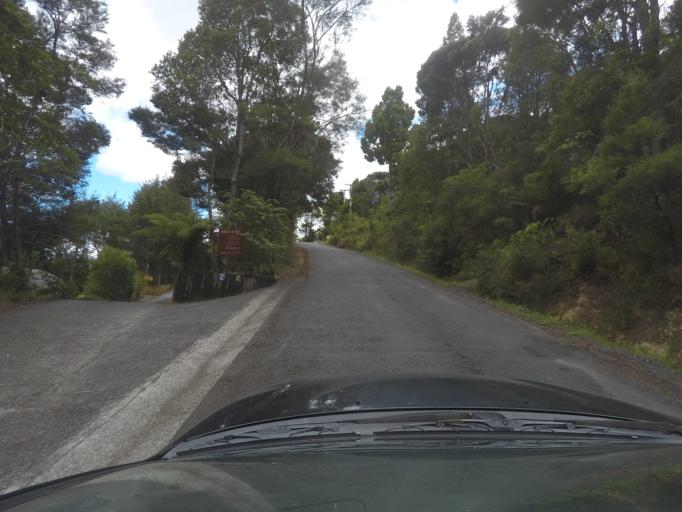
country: NZ
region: Northland
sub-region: Far North District
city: Paihia
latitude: -35.2897
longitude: 174.0970
